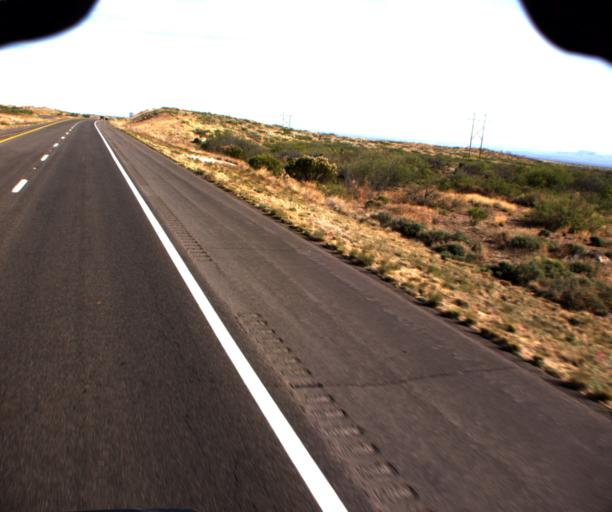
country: US
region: Arizona
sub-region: Graham County
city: Swift Trail Junction
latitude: 32.5036
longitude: -109.6738
